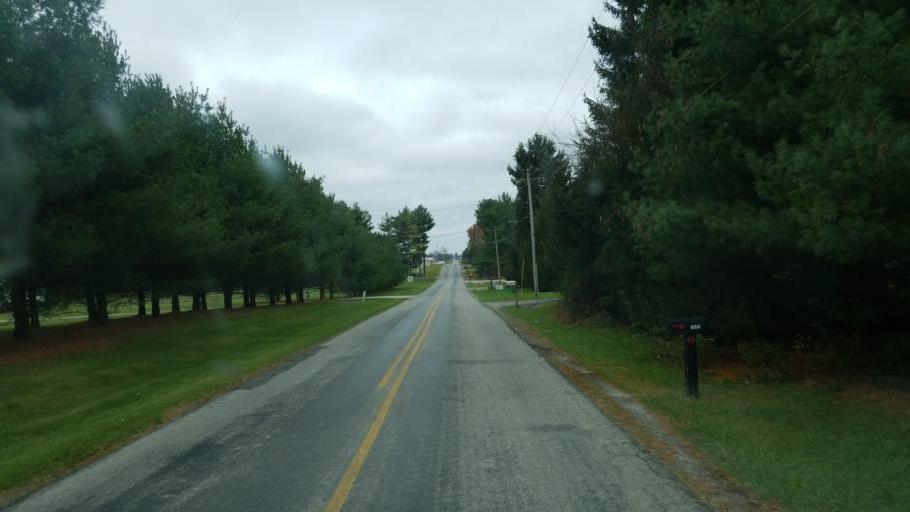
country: US
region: Ohio
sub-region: Licking County
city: Johnstown
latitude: 40.2007
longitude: -82.7564
